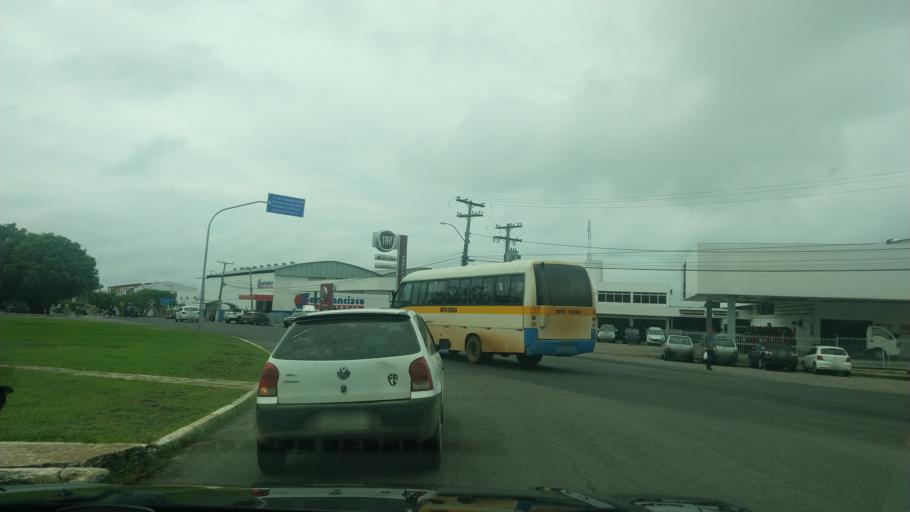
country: BR
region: Bahia
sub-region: Paulo Afonso
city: Paulo Afonso
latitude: -9.4014
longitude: -38.2391
